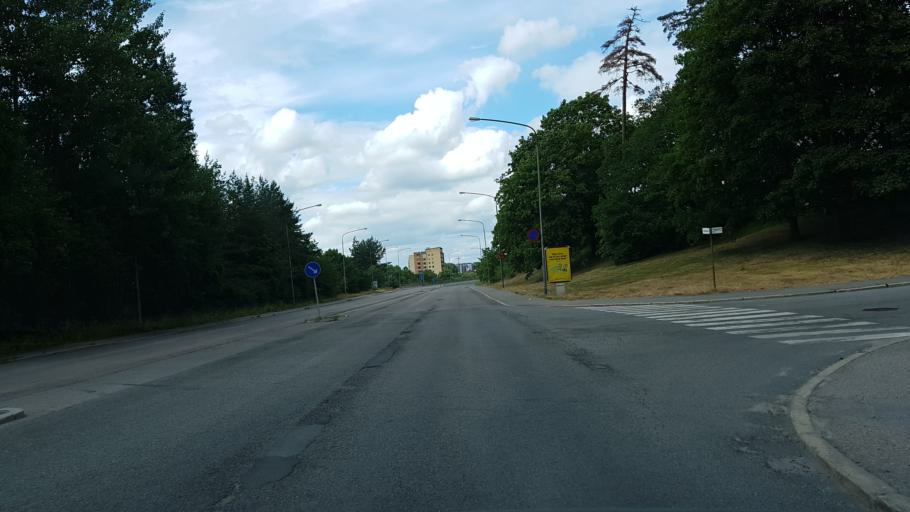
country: SE
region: Stockholm
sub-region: Solna Kommun
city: Solna
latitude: 59.3513
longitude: 17.9899
